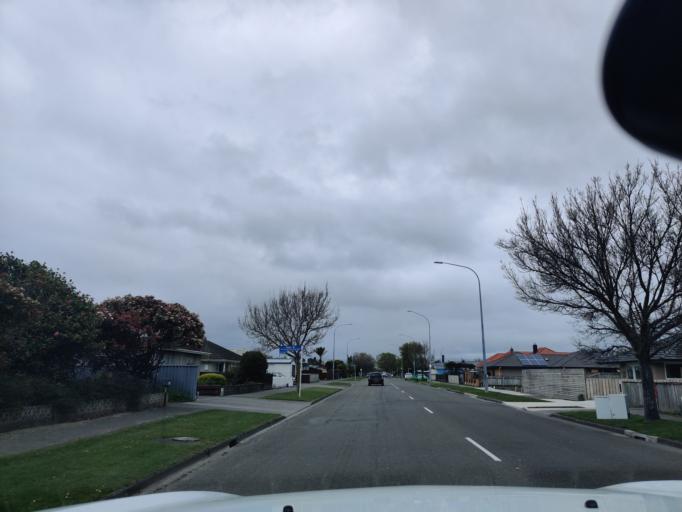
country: NZ
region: Manawatu-Wanganui
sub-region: Palmerston North City
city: Palmerston North
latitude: -40.3329
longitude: 175.6320
